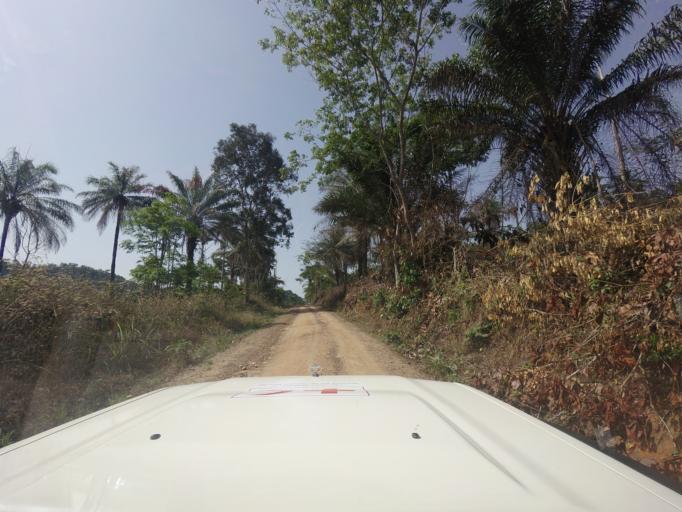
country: LR
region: Lofa
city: Voinjama
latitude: 8.4827
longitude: -9.7603
